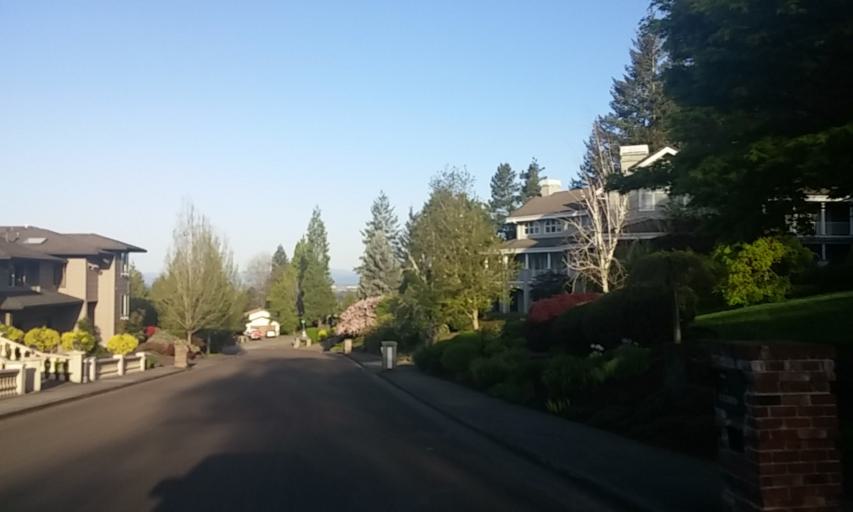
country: US
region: Oregon
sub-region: Washington County
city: Cedar Mill
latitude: 45.5431
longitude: -122.7937
